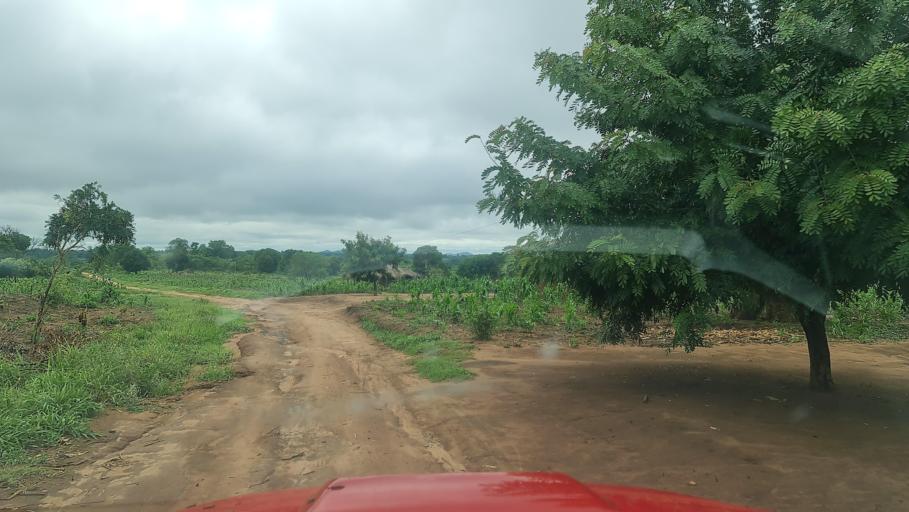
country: MW
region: Southern Region
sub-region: Nsanje District
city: Nsanje
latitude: -17.1933
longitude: 35.8591
